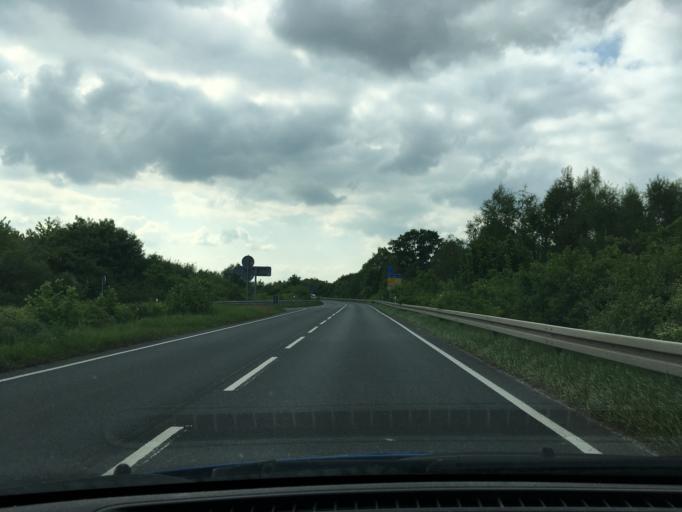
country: DE
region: Lower Saxony
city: Lehrte
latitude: 52.3911
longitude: 9.9675
